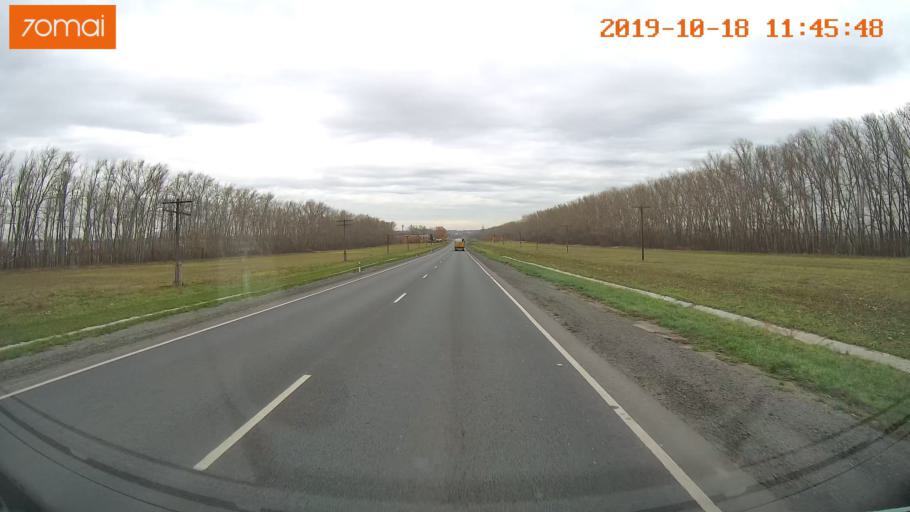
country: RU
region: Rjazan
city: Mikhaylov
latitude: 54.2137
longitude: 38.9749
